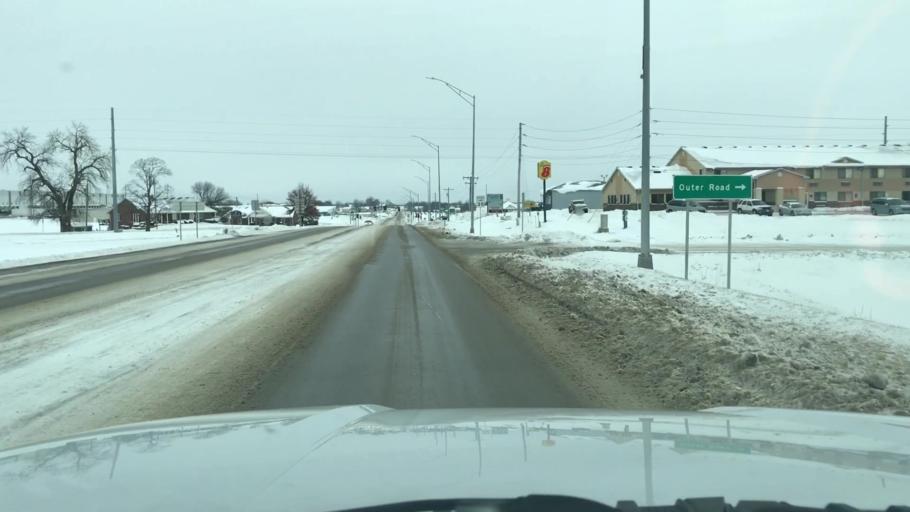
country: US
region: Missouri
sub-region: Clinton County
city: Cameron
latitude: 39.7557
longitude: -94.2343
